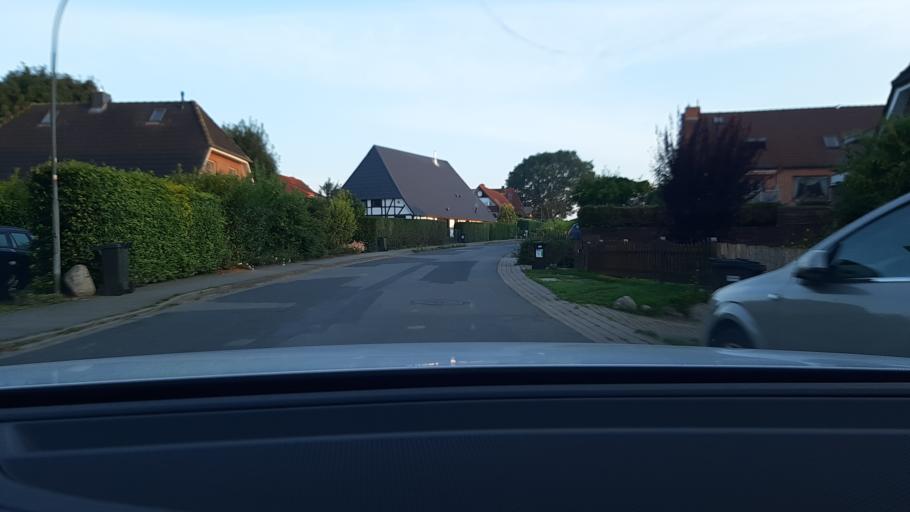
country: DE
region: Schleswig-Holstein
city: Klein Wesenberg
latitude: 53.8209
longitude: 10.5382
